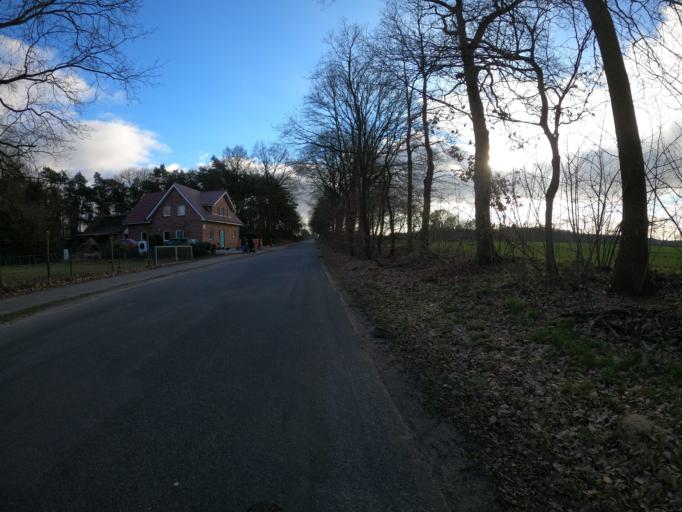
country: DE
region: Lower Saxony
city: Bawinkel
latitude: 52.6652
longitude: 7.3901
